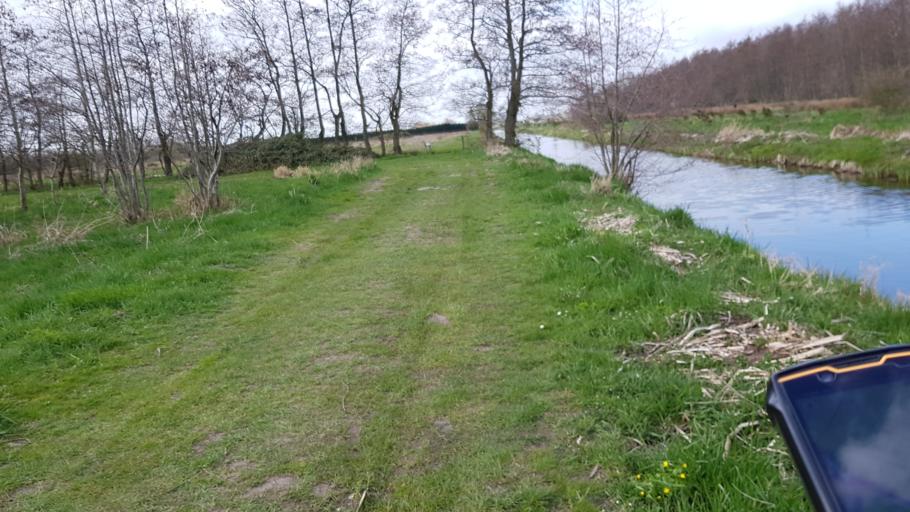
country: NL
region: Utrecht
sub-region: Gemeente Lopik
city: Lopik
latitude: 51.9529
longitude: 4.9973
